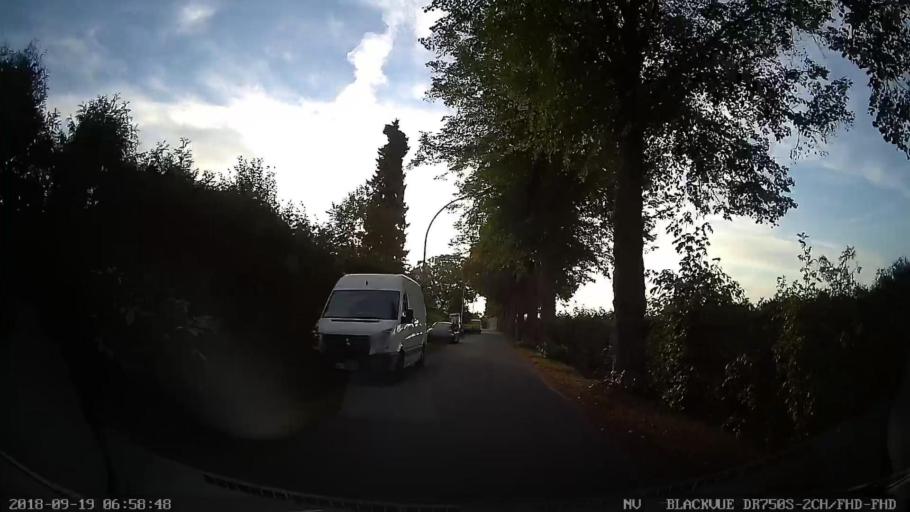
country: DE
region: Schleswig-Holstein
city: Ellerbek
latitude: 53.6329
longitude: 9.8848
